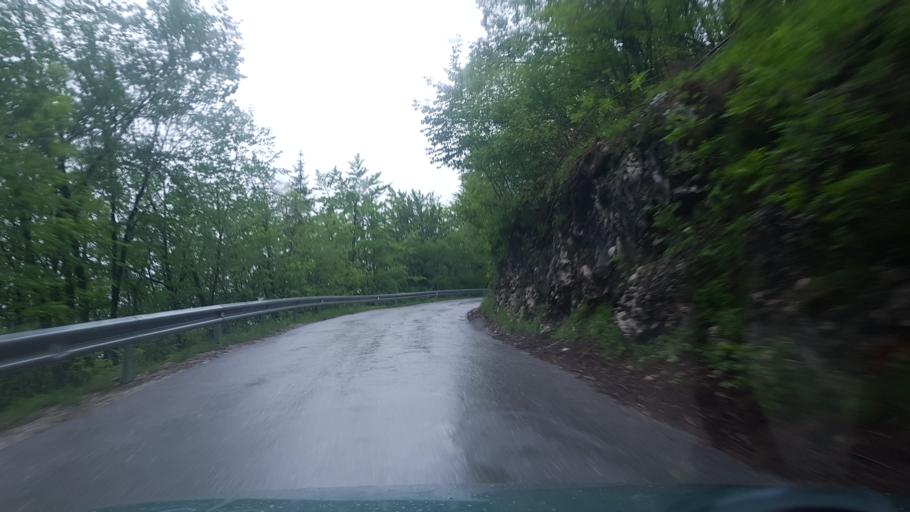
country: SI
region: Bohinj
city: Bohinjska Bistrica
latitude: 46.2732
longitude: 14.0052
